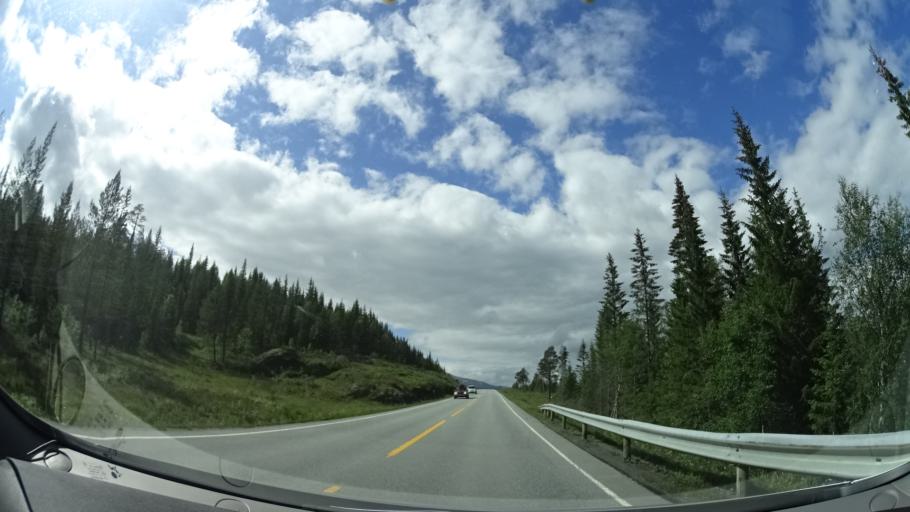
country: NO
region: Nord-Trondelag
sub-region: Meraker
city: Meraker
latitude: 63.3812
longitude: 11.8806
